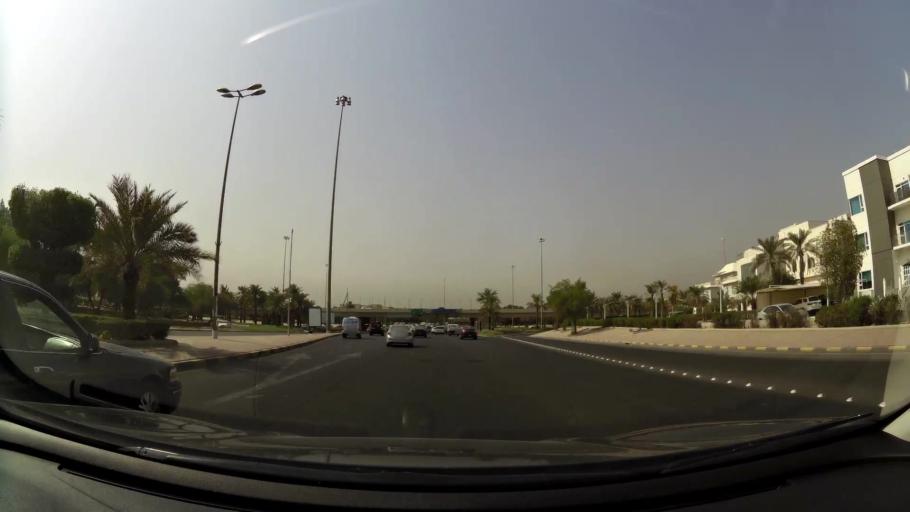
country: KW
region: Al Asimah
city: Ash Shamiyah
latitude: 29.3321
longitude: 47.9730
